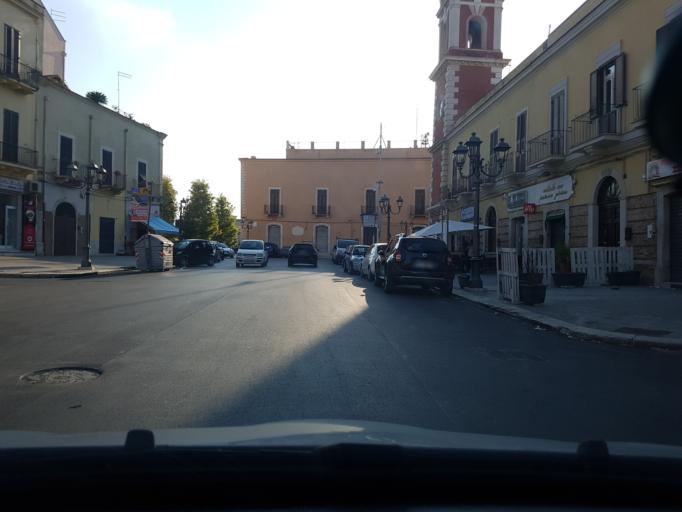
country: IT
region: Apulia
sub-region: Provincia di Foggia
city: Cerignola
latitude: 41.2657
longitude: 15.8943
